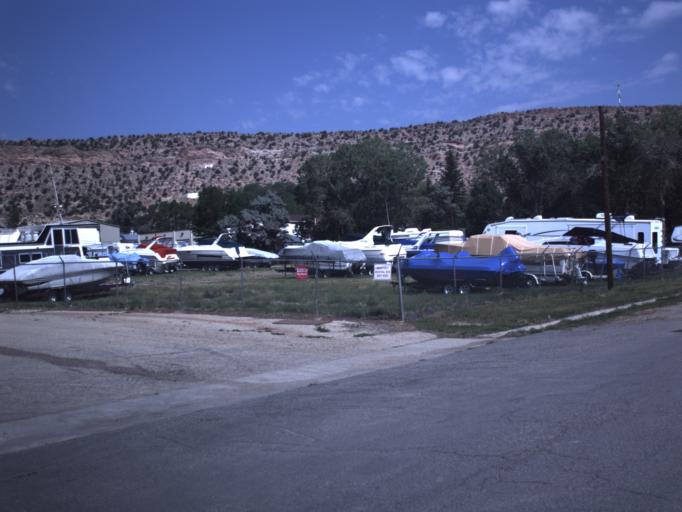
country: US
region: Utah
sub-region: Daggett County
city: Manila
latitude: 40.9886
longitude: -109.7227
